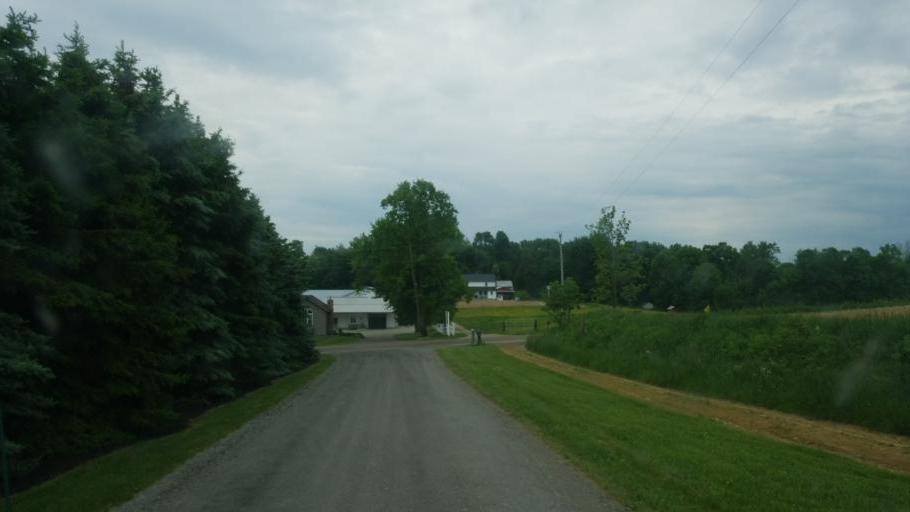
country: US
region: Ohio
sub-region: Tuscarawas County
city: Sugarcreek
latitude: 40.6192
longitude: -81.7405
